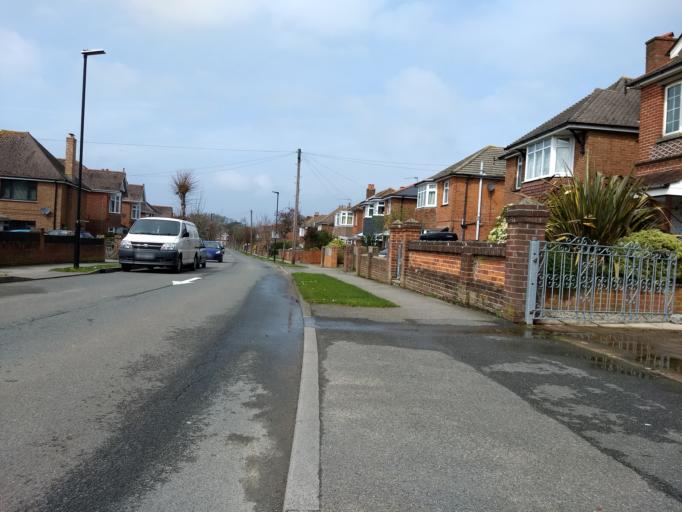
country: GB
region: England
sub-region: Isle of Wight
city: Ryde
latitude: 50.7249
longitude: -1.1731
